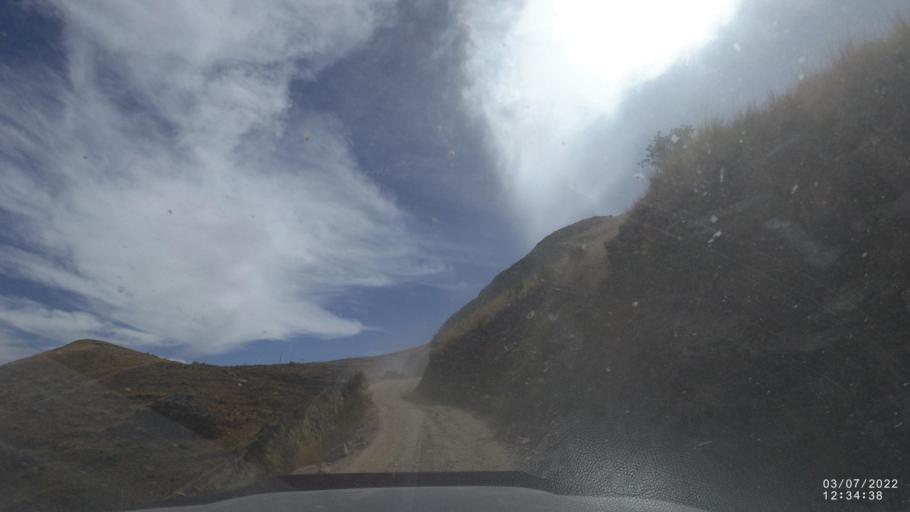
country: BO
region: Cochabamba
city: Irpa Irpa
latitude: -17.8066
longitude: -66.6067
